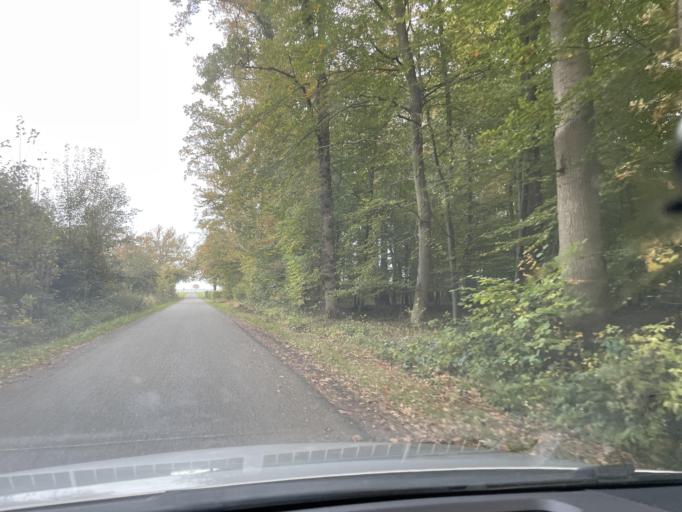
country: DK
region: South Denmark
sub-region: Kerteminde Kommune
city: Kerteminde
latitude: 55.4252
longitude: 10.6915
